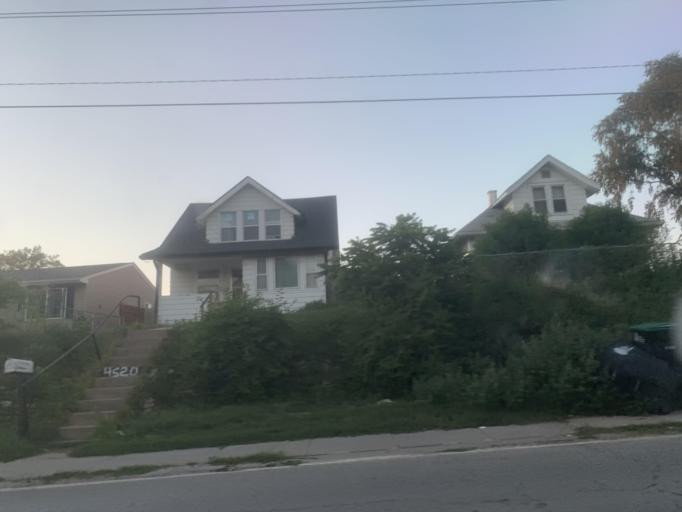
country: US
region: Nebraska
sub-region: Sarpy County
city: La Vista
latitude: 41.2053
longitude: -95.9826
